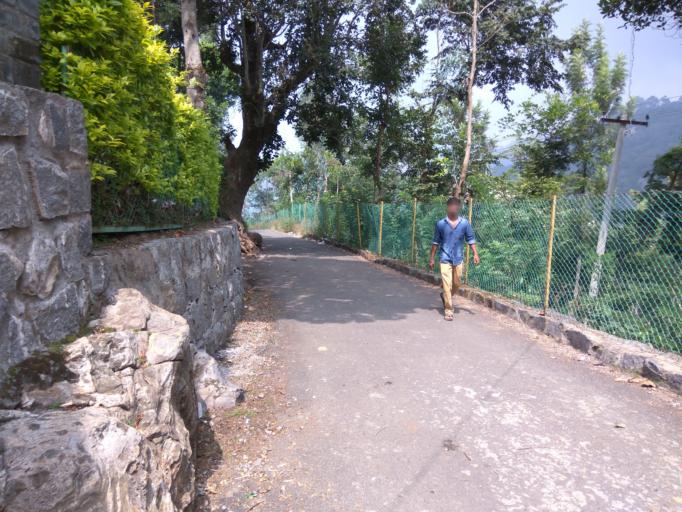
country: IN
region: Tamil Nadu
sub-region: Salem
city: Salem
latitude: 11.7945
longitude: 78.2012
